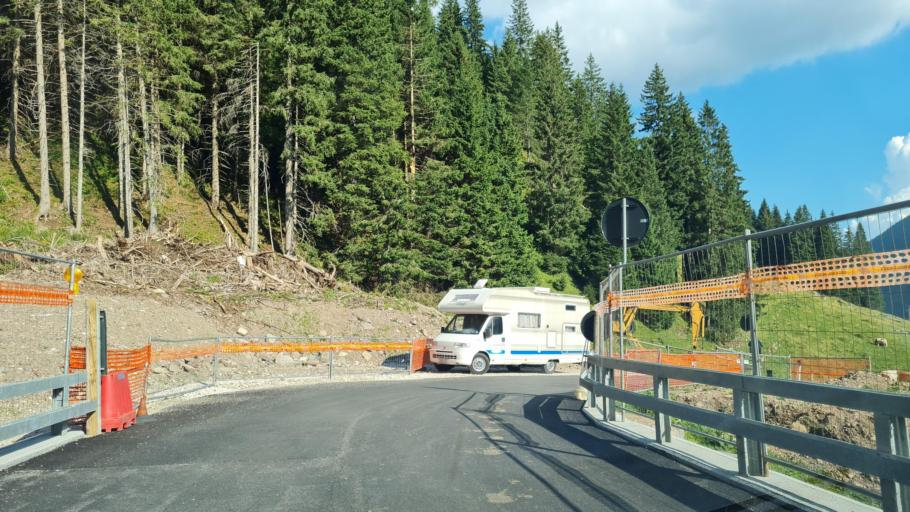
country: IT
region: Trentino-Alto Adige
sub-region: Provincia di Trento
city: Torcegno
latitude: 46.1600
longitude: 11.4351
